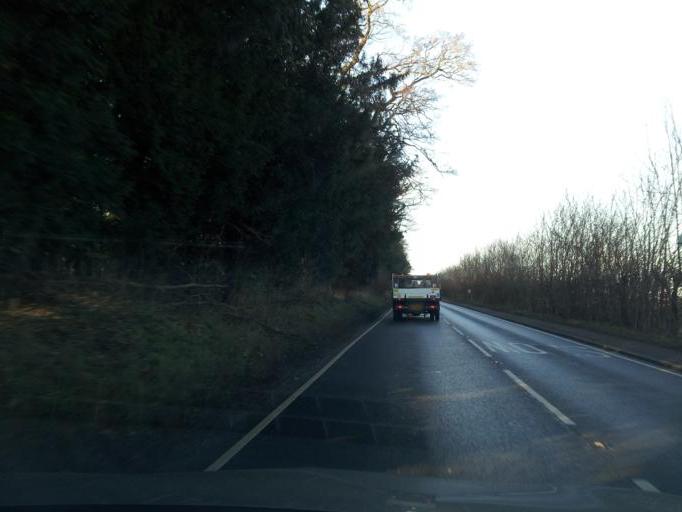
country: GB
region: England
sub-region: Suffolk
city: Bury St Edmunds
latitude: 52.2214
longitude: 0.7387
